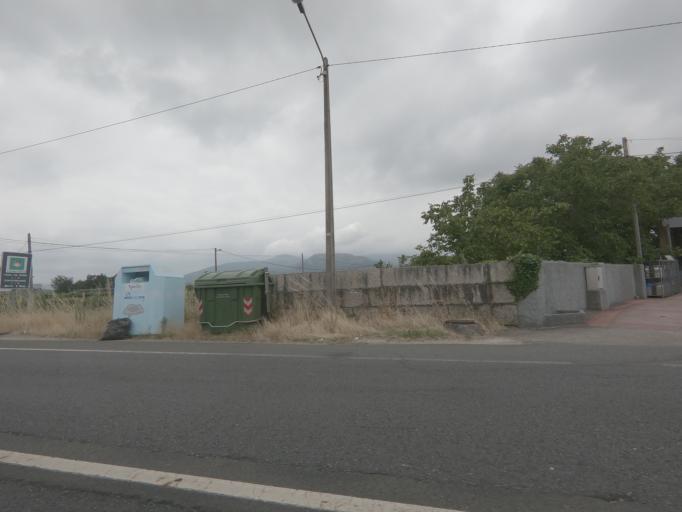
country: ES
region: Galicia
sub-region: Provincia de Pontevedra
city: Tomino
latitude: 41.9728
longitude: -8.7494
